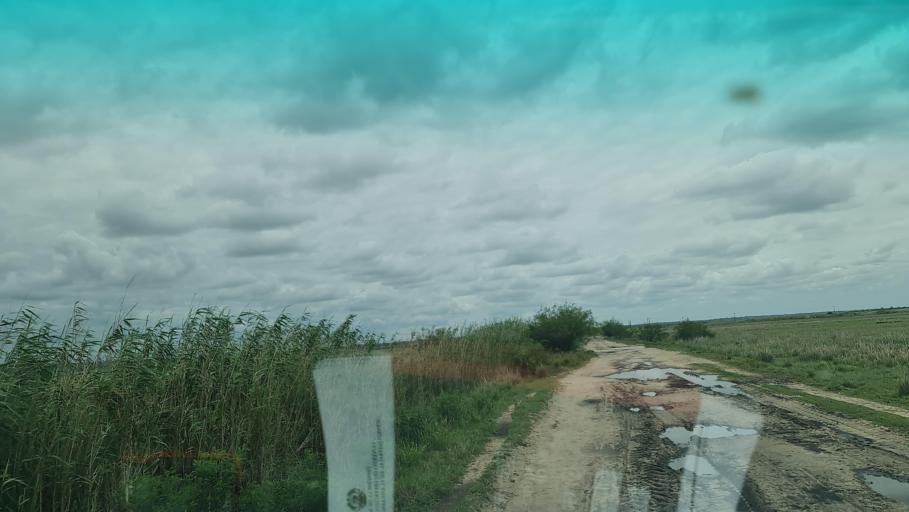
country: MZ
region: Maputo City
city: Maputo
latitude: -25.7273
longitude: 32.7022
